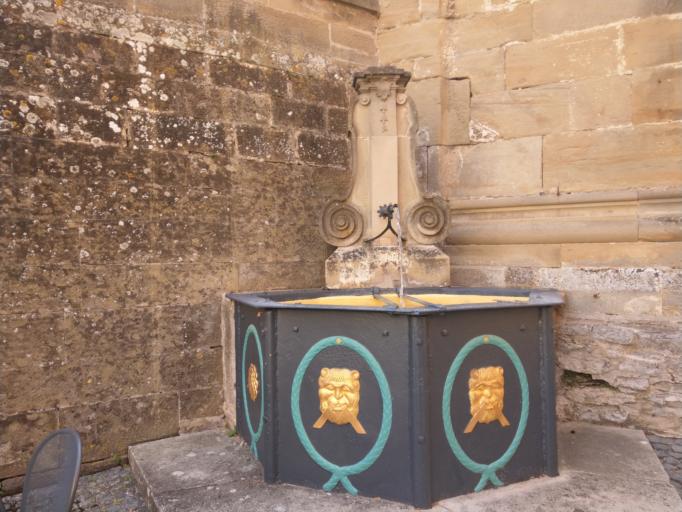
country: DE
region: Baden-Wuerttemberg
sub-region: Regierungsbezirk Stuttgart
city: Schwaebisch Hall
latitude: 49.1002
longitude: 9.7505
